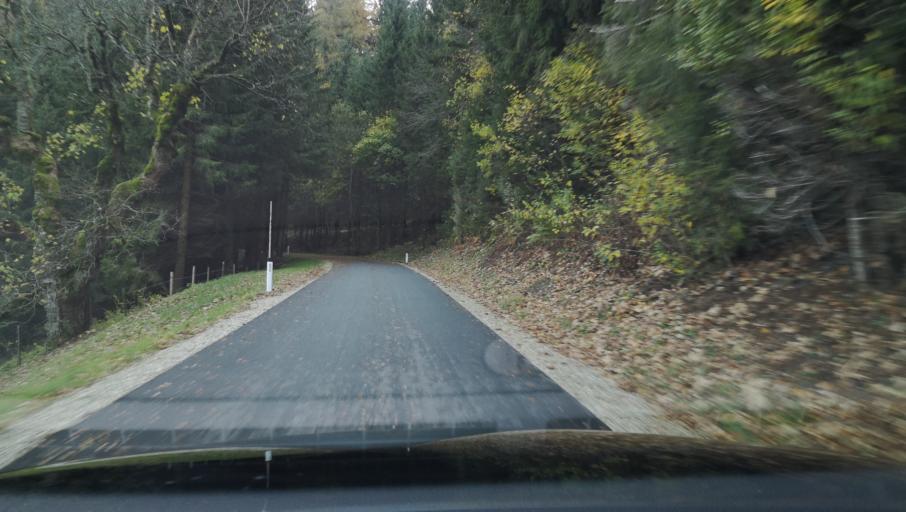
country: AT
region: Styria
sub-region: Politischer Bezirk Weiz
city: Gasen
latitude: 47.3571
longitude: 15.5900
